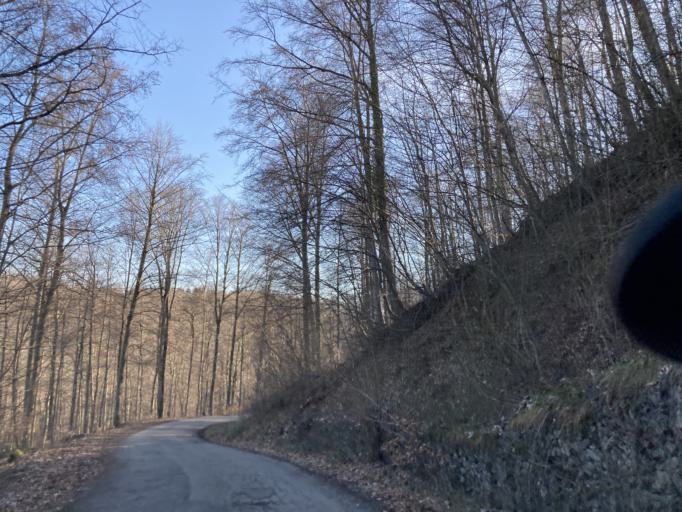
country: DE
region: Baden-Wuerttemberg
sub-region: Tuebingen Region
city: Ofterdingen
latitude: 48.3744
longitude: 9.0236
